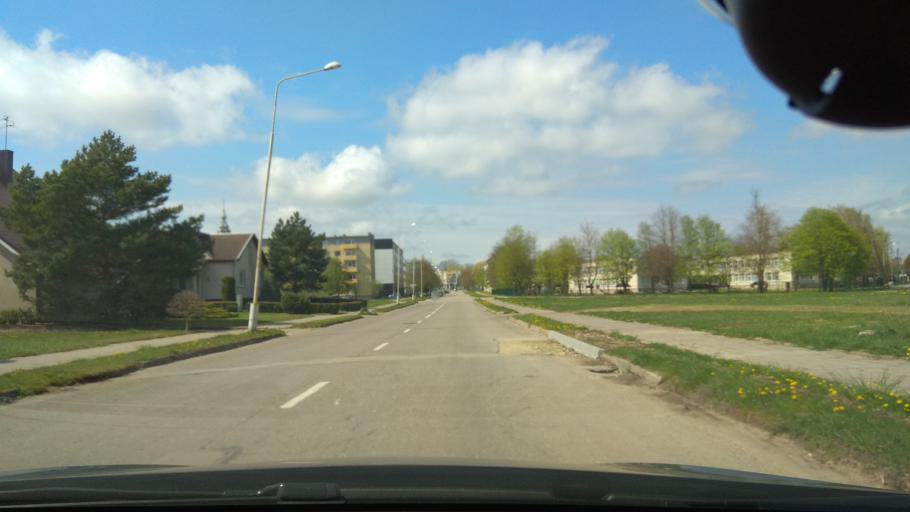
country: LT
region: Siauliu apskritis
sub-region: Joniskis
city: Joniskis
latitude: 56.2420
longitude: 23.6241
